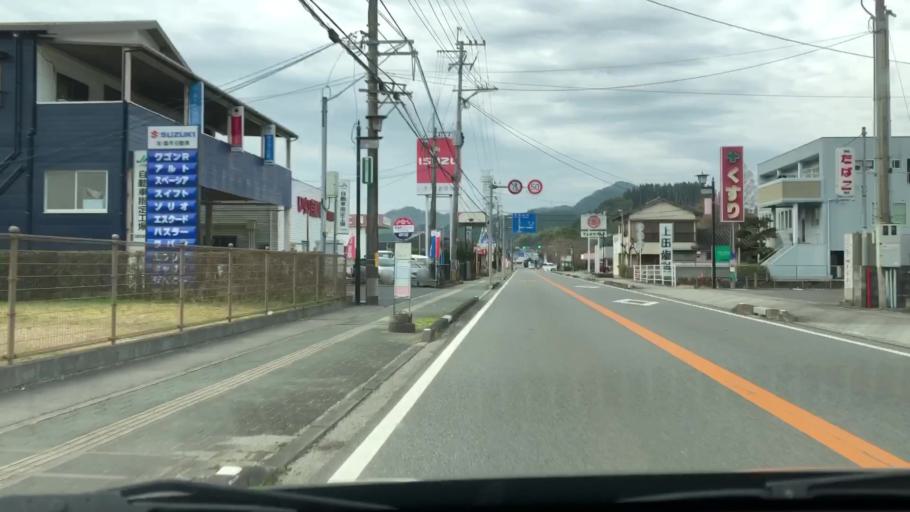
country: JP
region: Oita
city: Saiki
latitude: 32.9722
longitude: 131.8411
